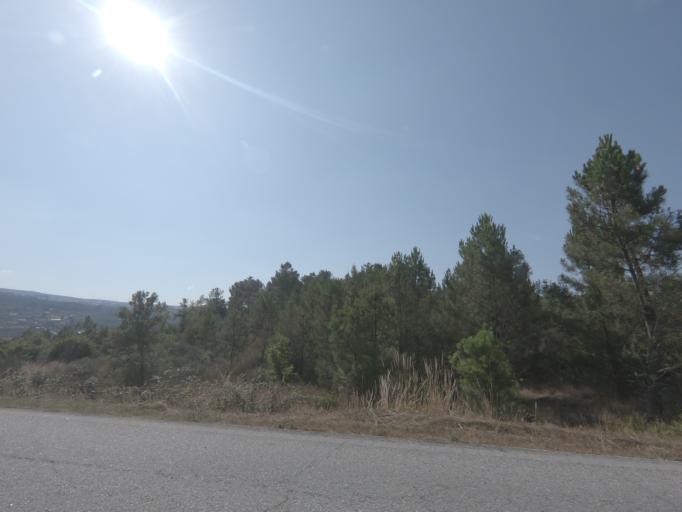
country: PT
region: Viseu
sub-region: Moimenta da Beira
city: Moimenta da Beira
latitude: 40.9797
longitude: -7.5778
